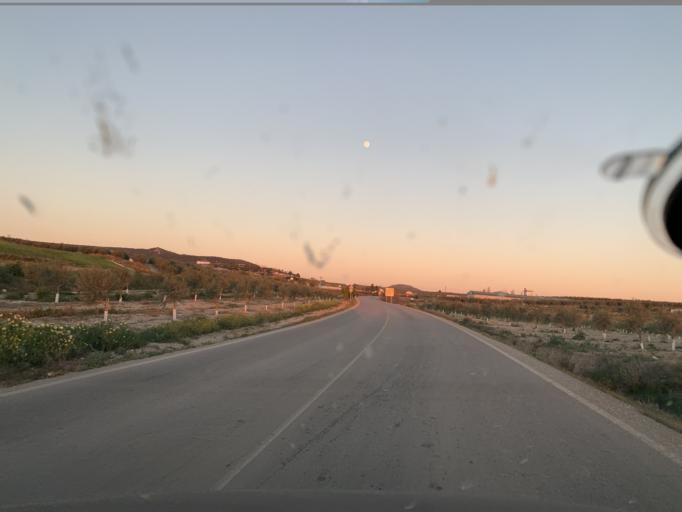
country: ES
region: Andalusia
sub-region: Provincia de Sevilla
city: Gilena
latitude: 37.2435
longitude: -4.9219
